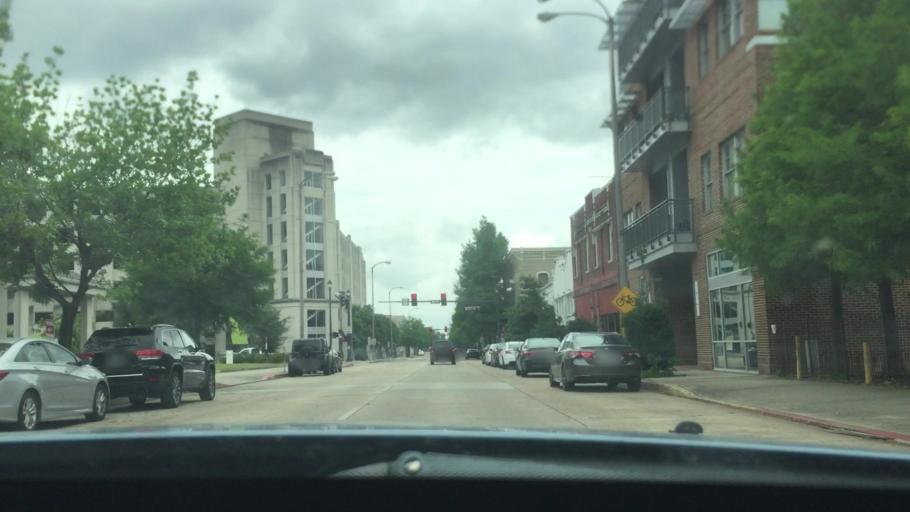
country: US
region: Louisiana
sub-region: West Baton Rouge Parish
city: Port Allen
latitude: 30.4515
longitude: -91.1869
